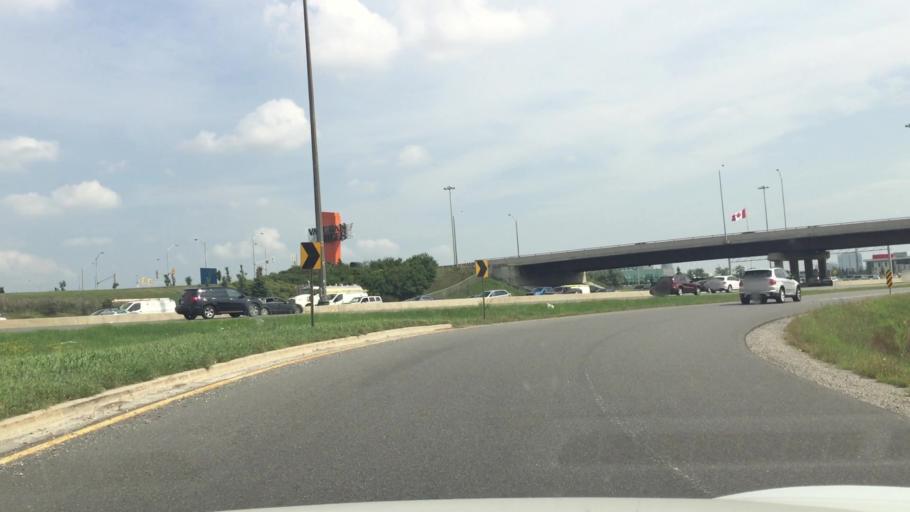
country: CA
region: Ontario
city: Vaughan
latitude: 43.8219
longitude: -79.5464
